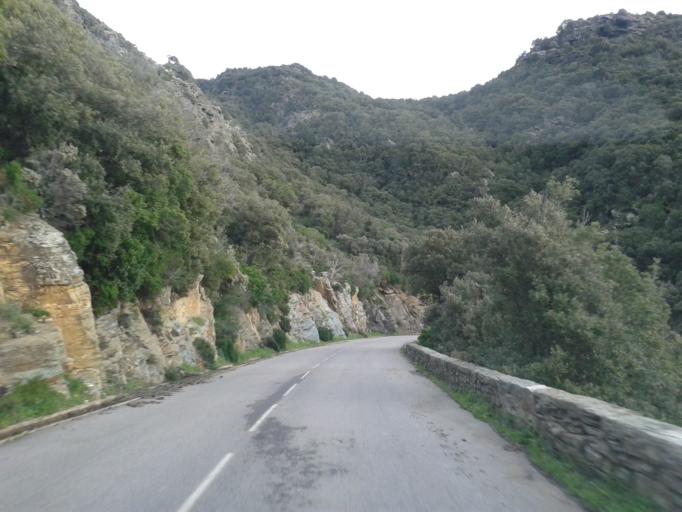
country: FR
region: Corsica
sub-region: Departement de la Haute-Corse
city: Brando
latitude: 42.8842
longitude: 9.3341
